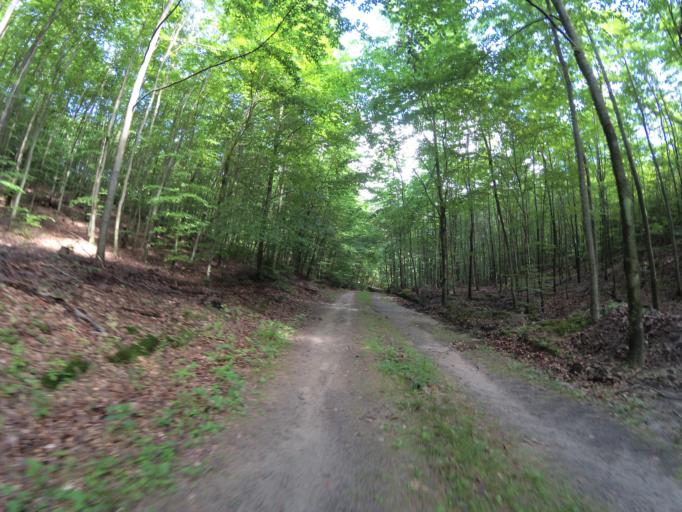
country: PL
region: Pomeranian Voivodeship
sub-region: Gdynia
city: Wielki Kack
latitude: 54.5119
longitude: 18.4521
